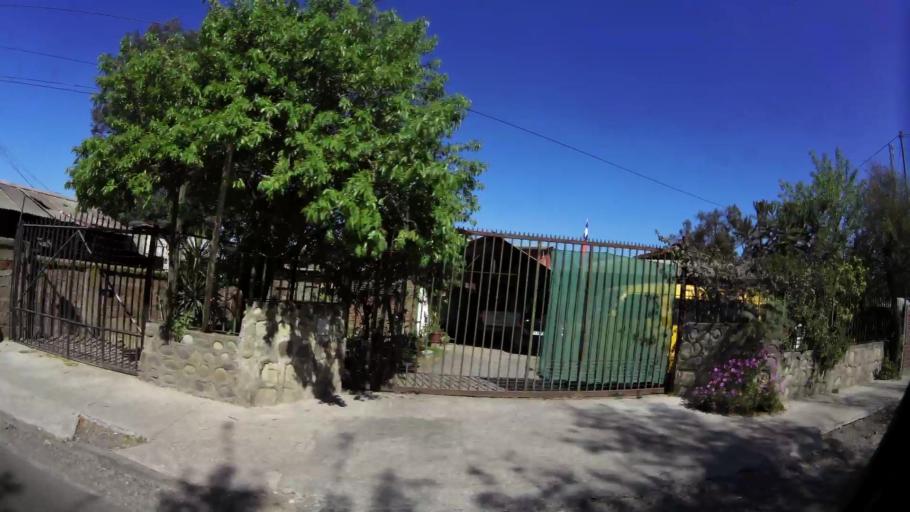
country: CL
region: Santiago Metropolitan
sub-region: Provincia de Talagante
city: Penaflor
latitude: -33.6103
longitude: -70.8969
